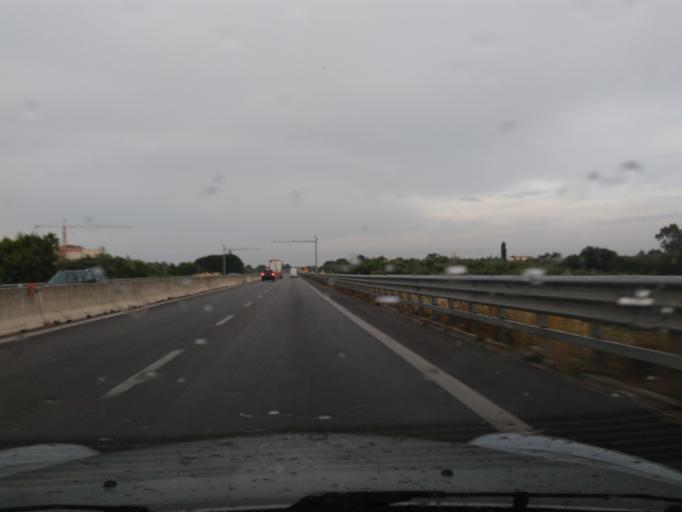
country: IT
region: Apulia
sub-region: Provincia di Bari
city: Molfetta
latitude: 41.1851
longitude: 16.5923
